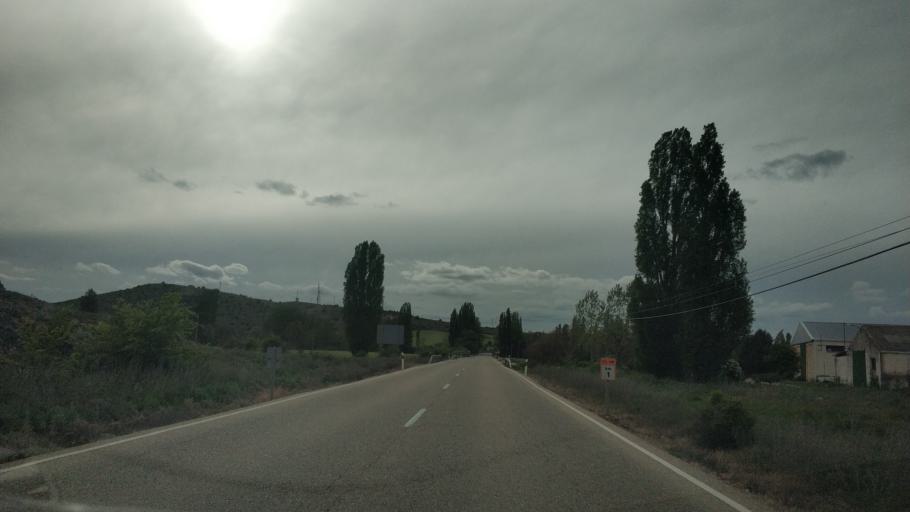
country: ES
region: Castille and Leon
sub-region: Provincia de Soria
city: El Burgo de Osma
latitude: 41.5793
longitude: -3.0350
